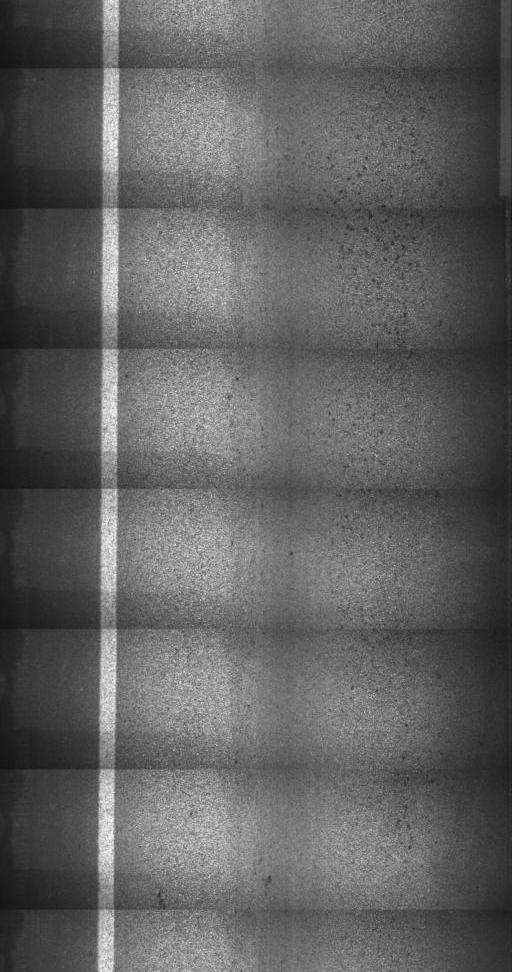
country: US
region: Vermont
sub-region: Windsor County
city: Springfield
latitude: 43.3521
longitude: -72.5245
